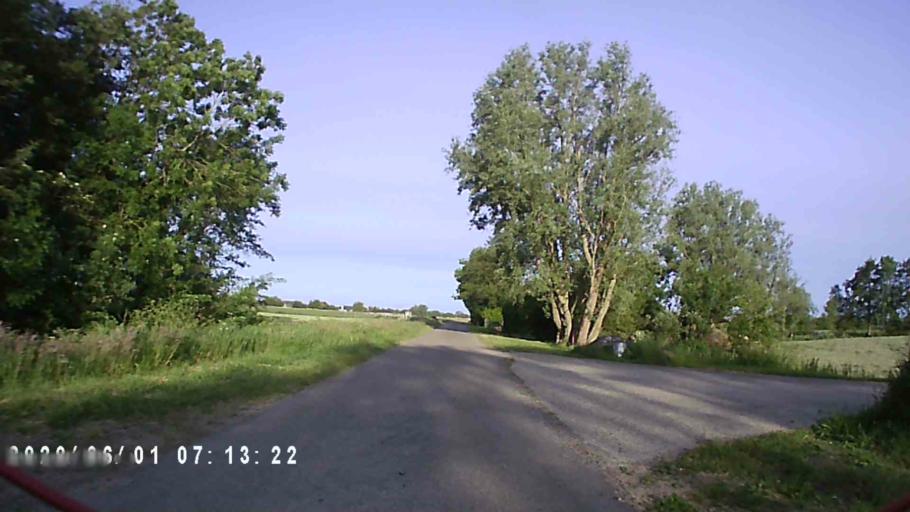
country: NL
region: Friesland
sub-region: Gemeente Dantumadiel
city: Walterswald
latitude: 53.3135
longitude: 6.0588
